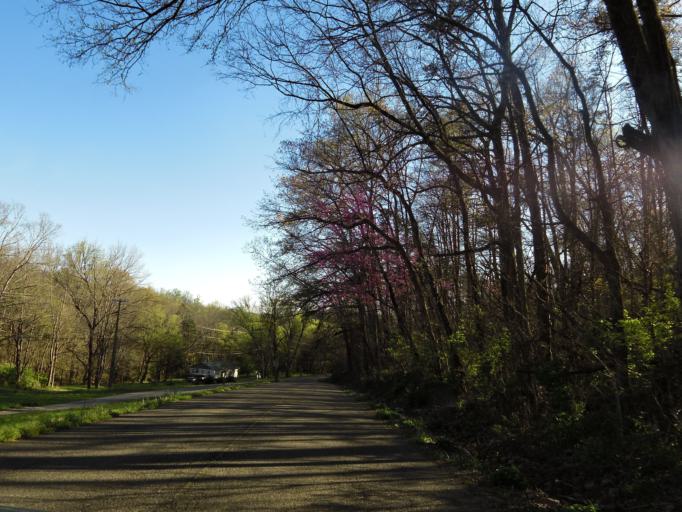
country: US
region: Tennessee
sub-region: Knox County
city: Mascot
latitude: 35.9750
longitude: -83.7531
